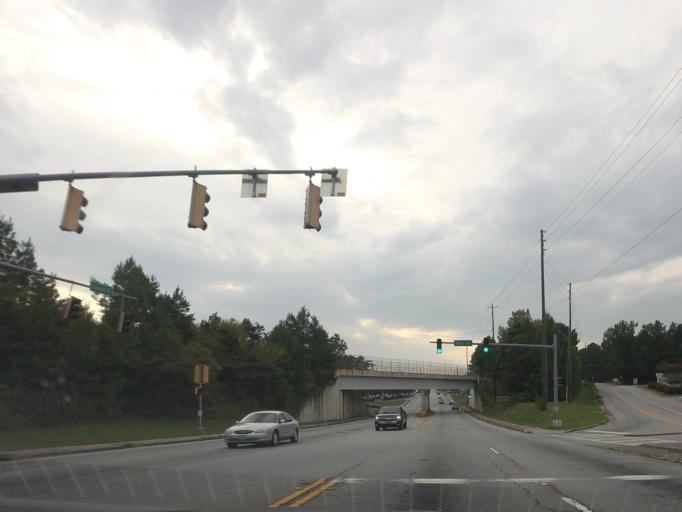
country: US
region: Georgia
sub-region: Bibb County
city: Macon
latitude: 32.8679
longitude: -83.6972
